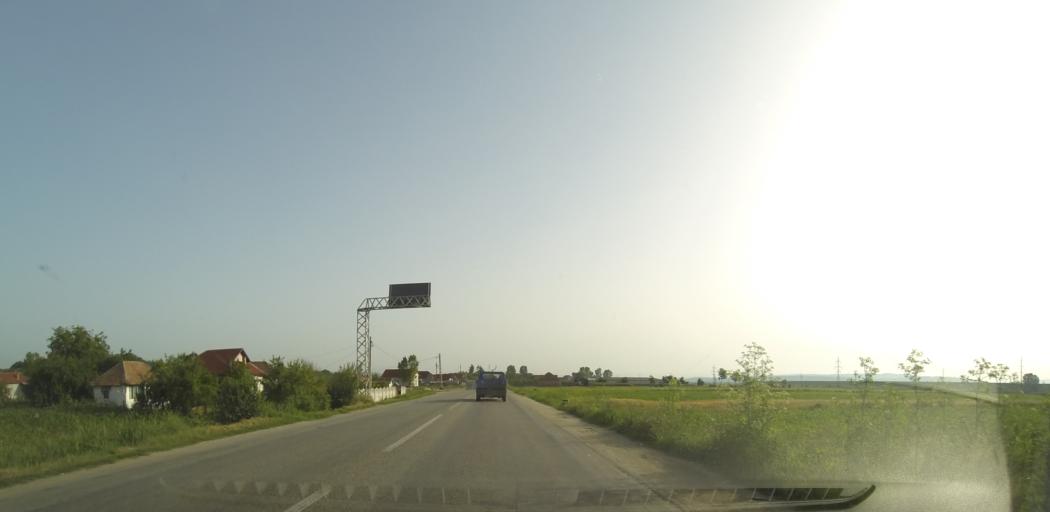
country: RO
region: Valcea
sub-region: Comuna Babeni
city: Valea Mare
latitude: 44.9316
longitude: 24.2361
